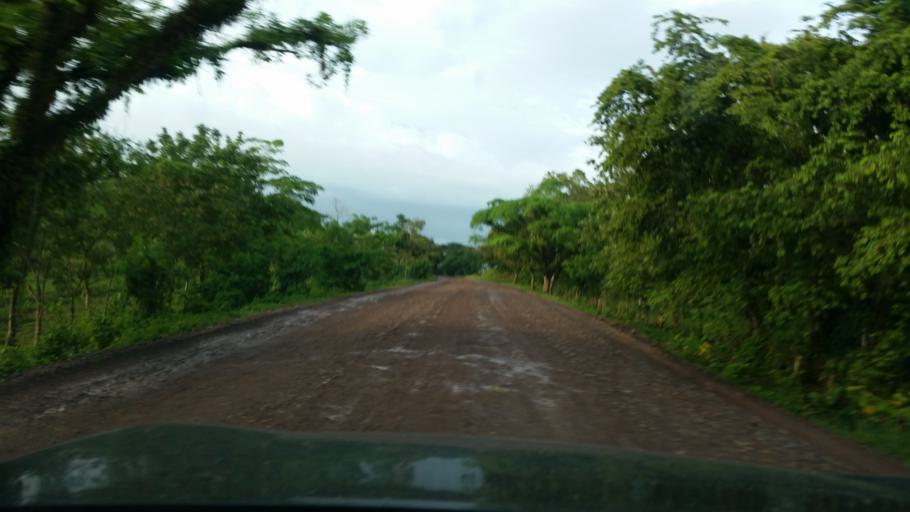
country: NI
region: Atlantico Norte (RAAN)
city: Siuna
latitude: 13.3604
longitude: -84.8854
